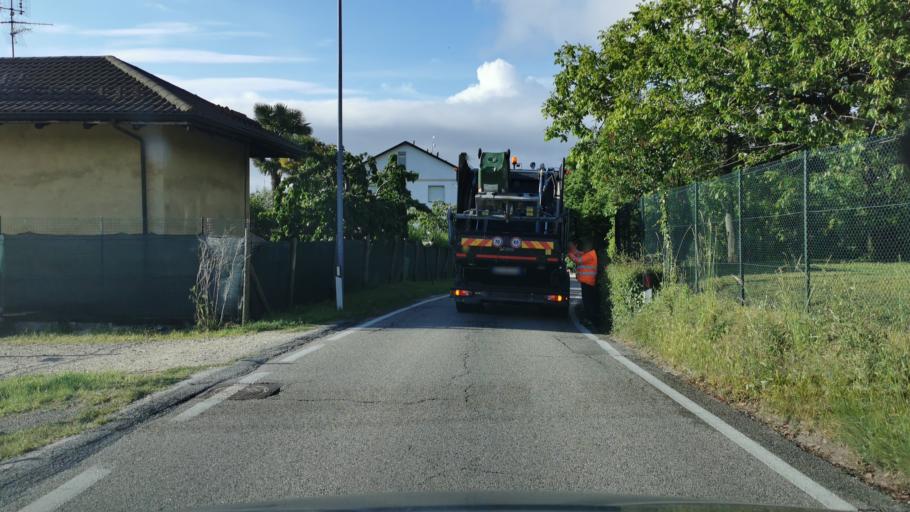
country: IT
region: Piedmont
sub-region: Provincia di Torino
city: Pino Torinese
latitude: 45.0323
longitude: 7.7732
